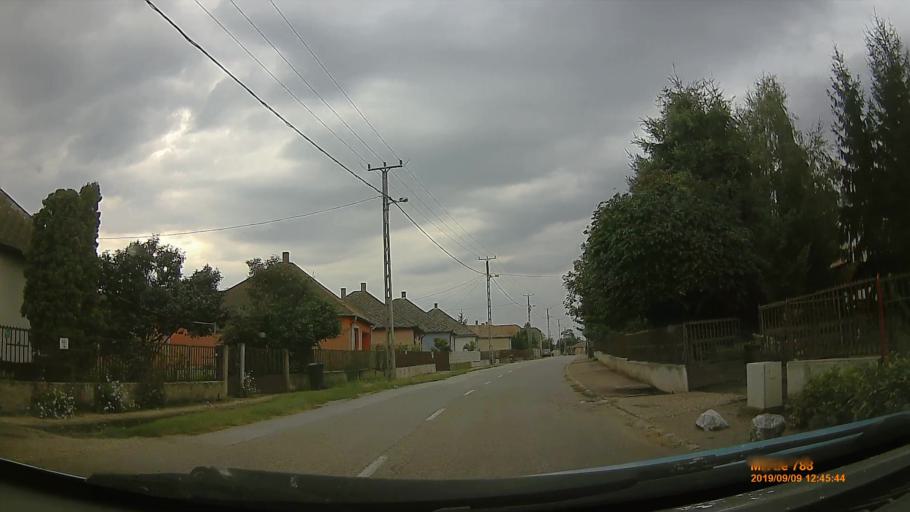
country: HU
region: Szabolcs-Szatmar-Bereg
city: Nyirpazony
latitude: 47.9530
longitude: 21.8053
